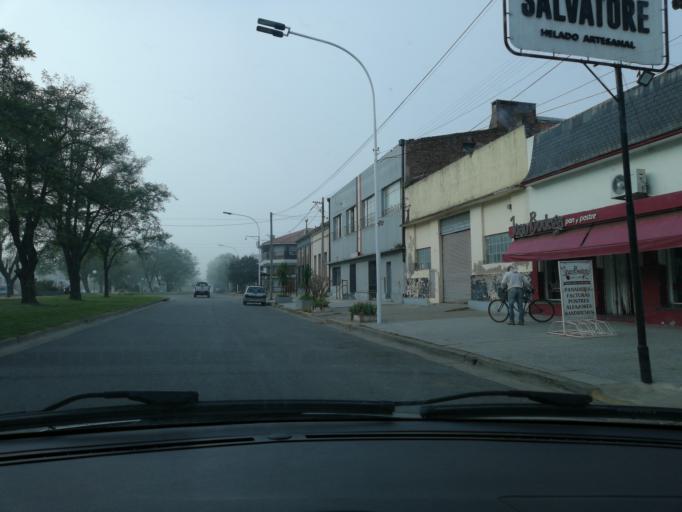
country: AR
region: Buenos Aires
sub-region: Partido de Balcarce
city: Balcarce
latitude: -37.8524
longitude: -58.2486
